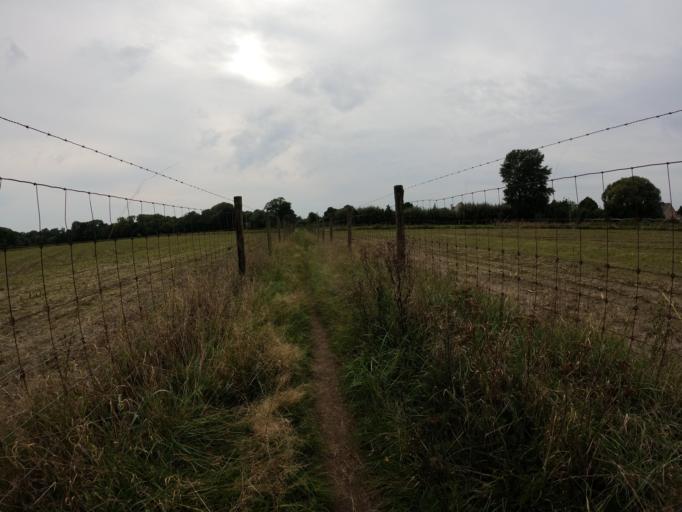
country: BE
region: Flanders
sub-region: Provincie Antwerpen
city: Wommelgem
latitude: 51.2061
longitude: 4.5346
